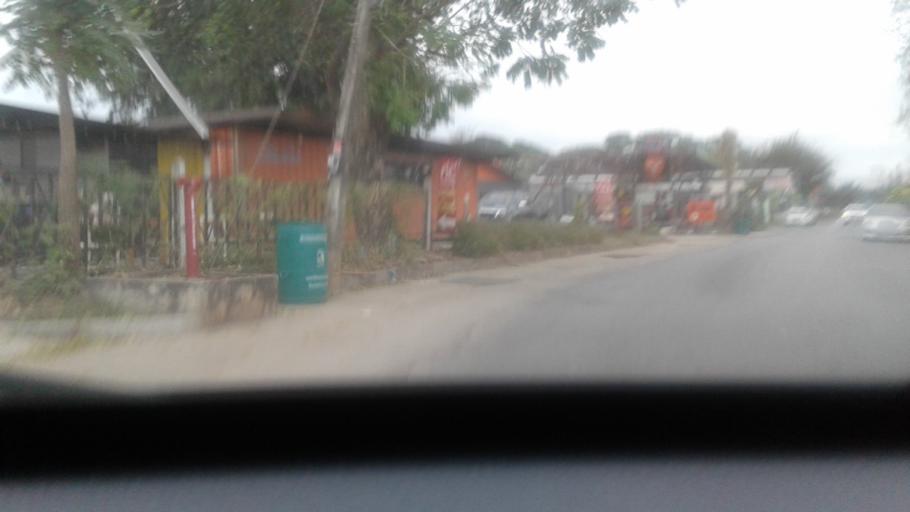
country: TH
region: Changwat Udon Thani
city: Udon Thani
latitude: 17.3981
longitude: 102.7853
